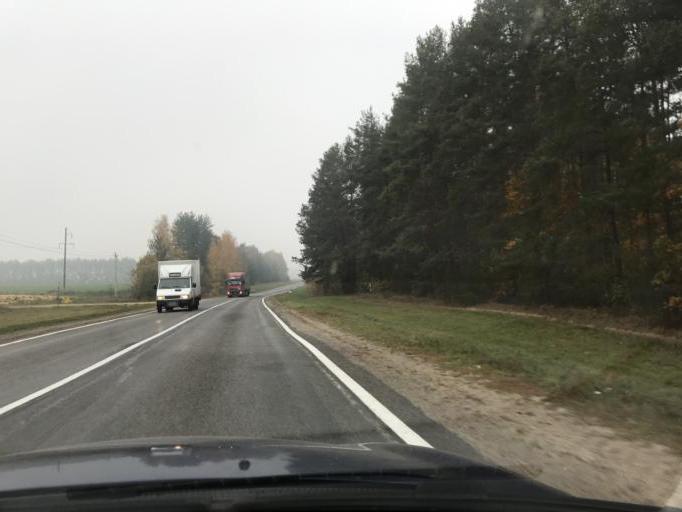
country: BY
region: Grodnenskaya
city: Hrodna
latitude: 53.7842
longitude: 23.8508
